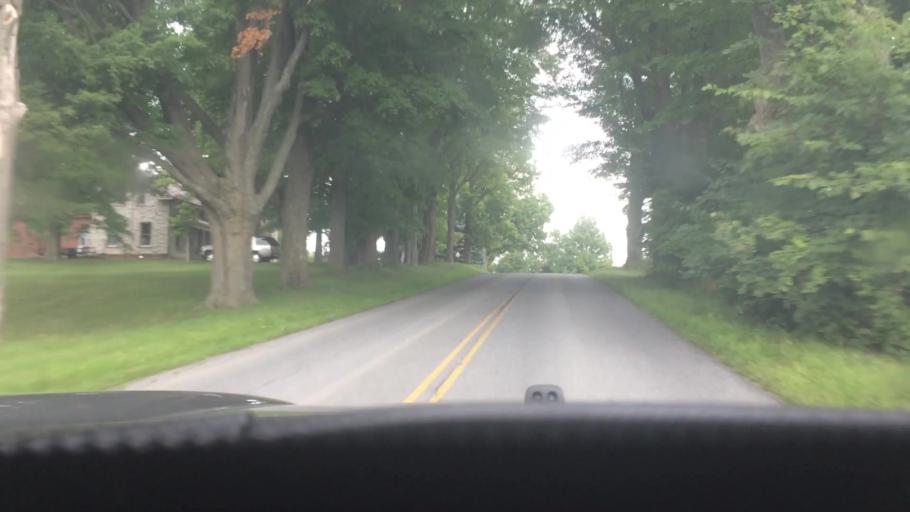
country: US
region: New York
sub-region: St. Lawrence County
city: Canton
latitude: 44.5564
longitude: -75.1278
